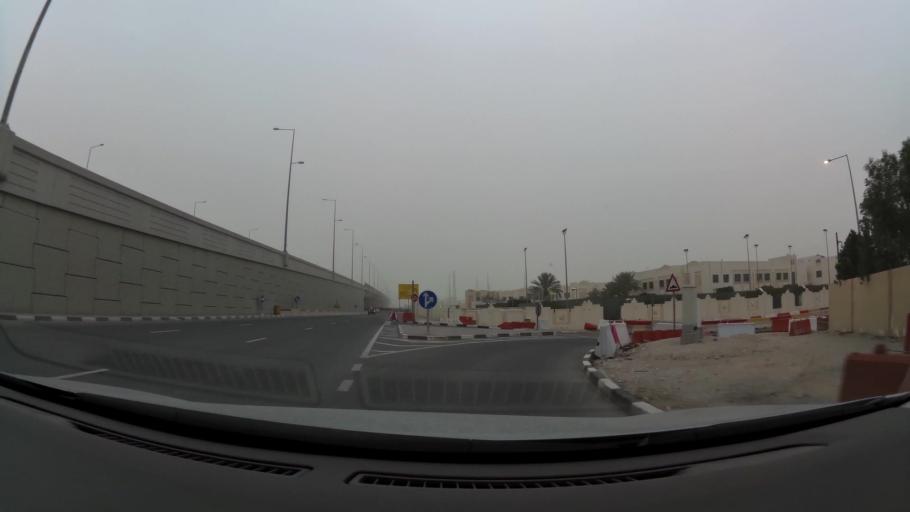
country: QA
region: Baladiyat ad Dawhah
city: Doha
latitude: 25.2327
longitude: 51.5030
